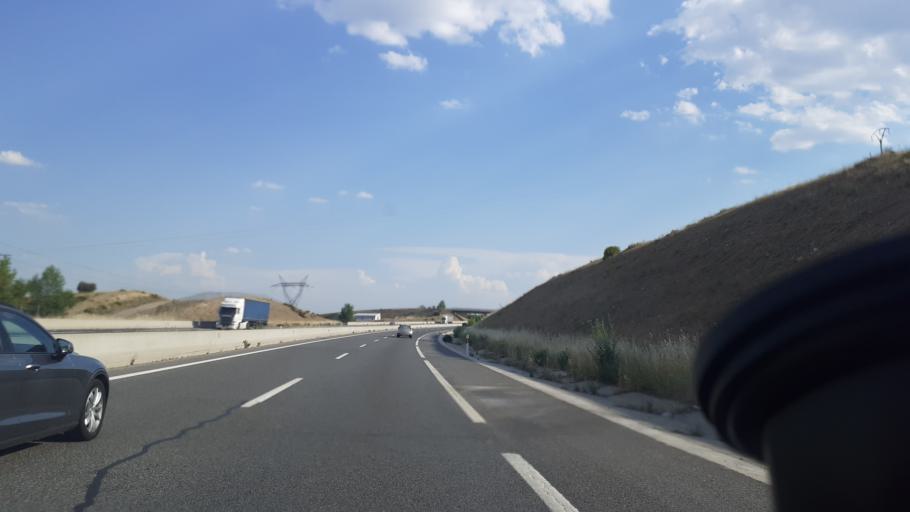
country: ES
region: Madrid
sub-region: Provincia de Madrid
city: El Molar
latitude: 40.7374
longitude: -3.5679
